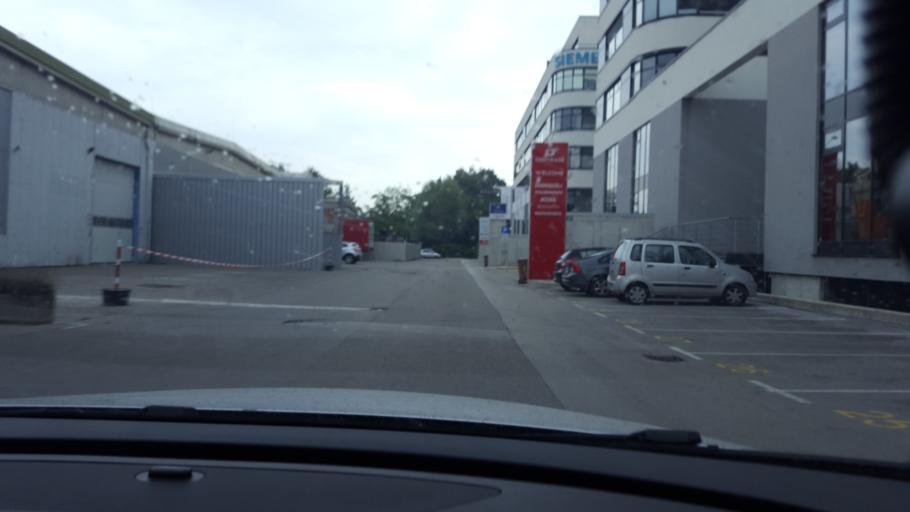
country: SI
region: Dol pri Ljubljani
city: Dol pri Ljubljani
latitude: 46.0633
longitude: 14.5658
